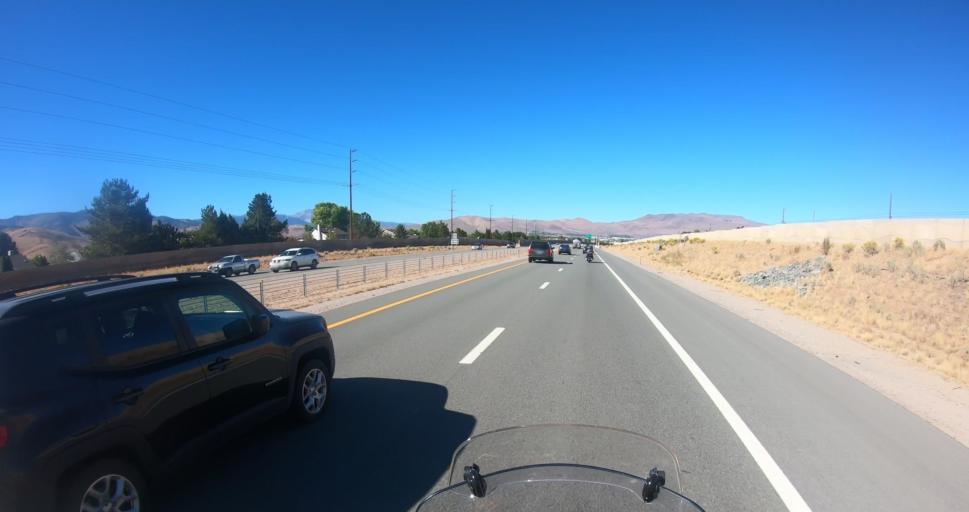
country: US
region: Nevada
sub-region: Carson City
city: Carson City
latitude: 39.1409
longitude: -119.7466
